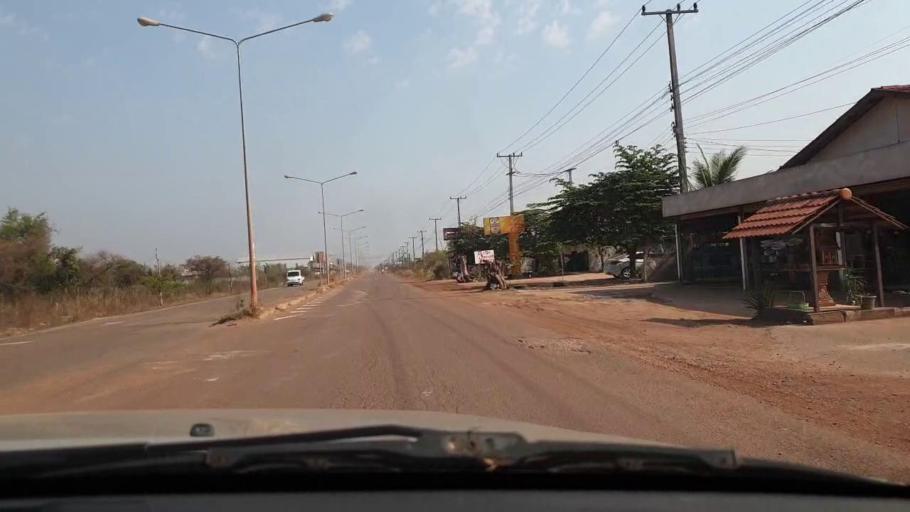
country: LA
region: Vientiane
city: Vientiane
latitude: 18.0055
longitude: 102.7200
